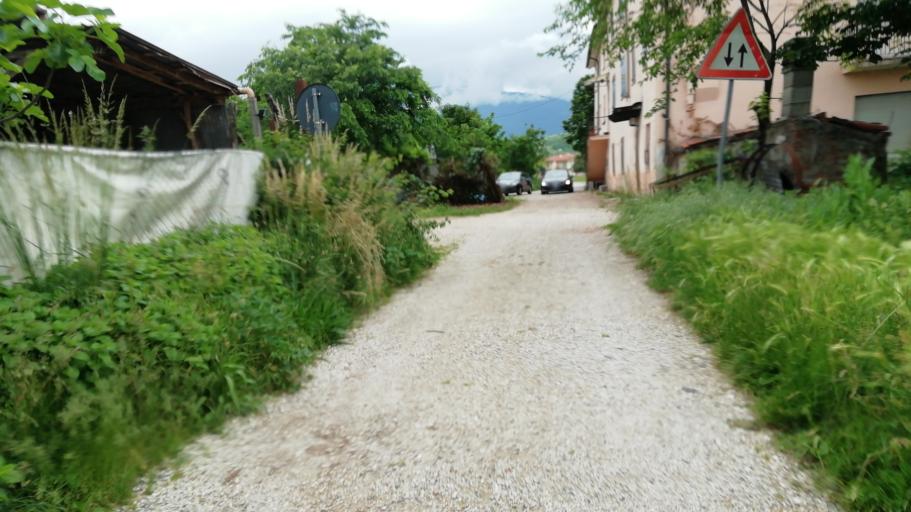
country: IT
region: Veneto
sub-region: Provincia di Vicenza
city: Centrale
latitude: 45.7206
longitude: 11.4785
